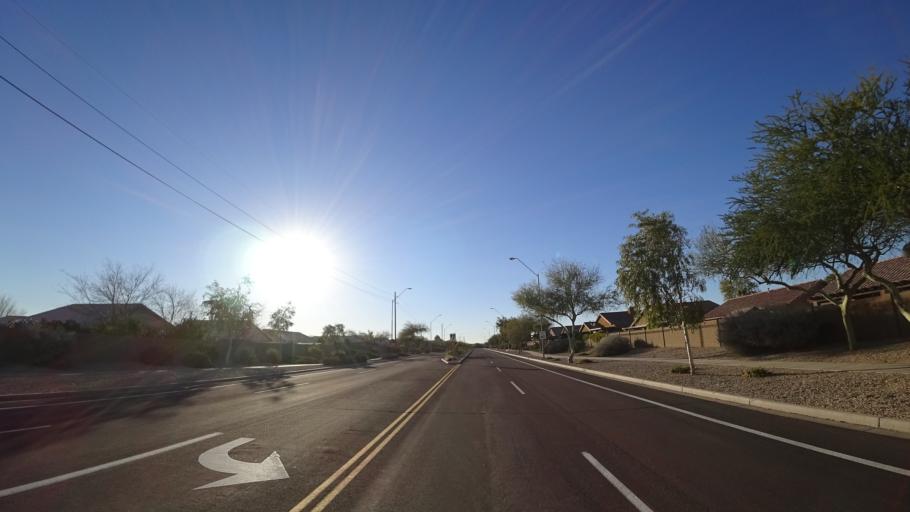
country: US
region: Arizona
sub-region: Maricopa County
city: Sun City West
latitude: 33.6818
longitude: -112.2903
